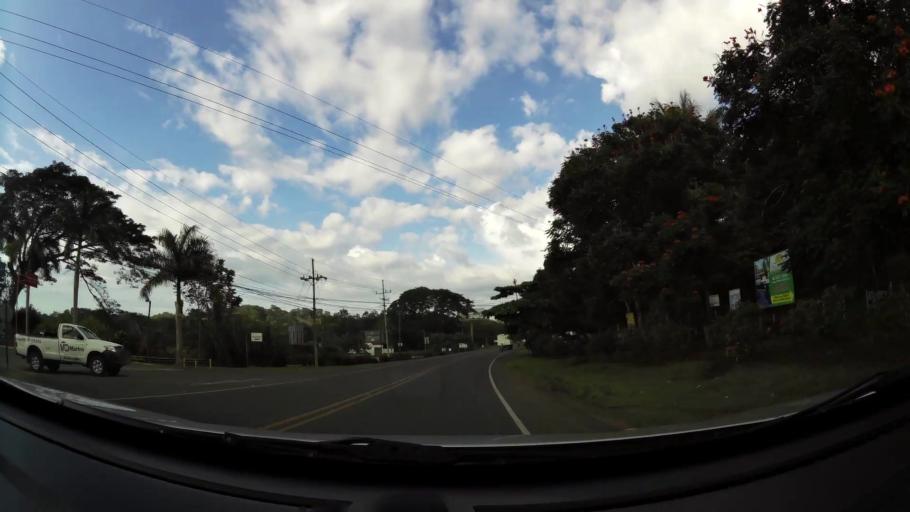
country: CR
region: Puntarenas
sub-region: Canton de Garabito
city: Jaco
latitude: 9.7118
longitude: -84.6359
